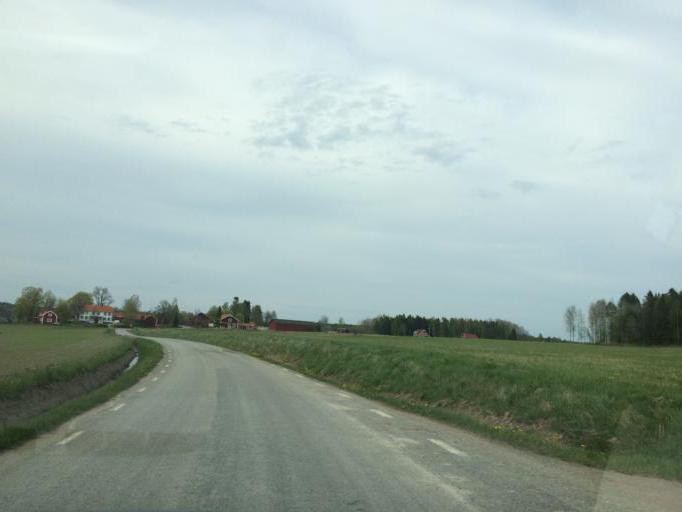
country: SE
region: Vaestmanland
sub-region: Kopings Kommun
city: Koping
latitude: 59.6102
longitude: 16.0285
